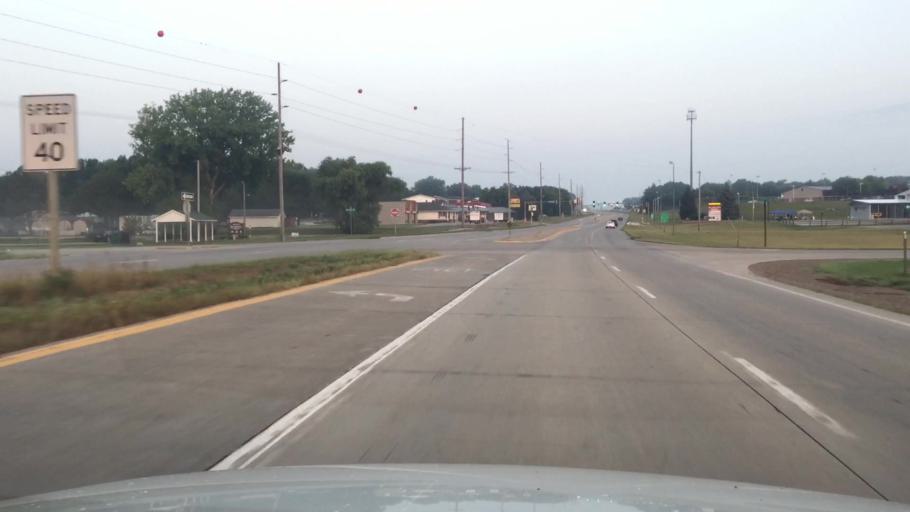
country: US
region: Iowa
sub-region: Warren County
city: Carlisle
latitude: 41.4934
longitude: -93.4843
